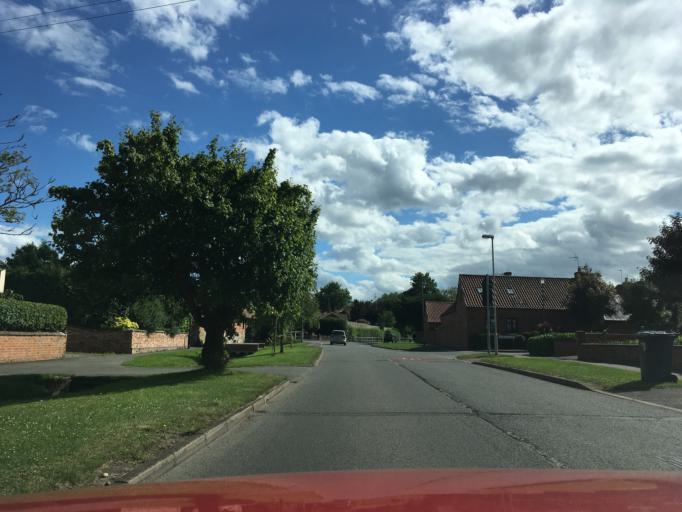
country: GB
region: England
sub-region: Nottinghamshire
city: East Leake
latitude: 52.8299
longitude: -1.1823
